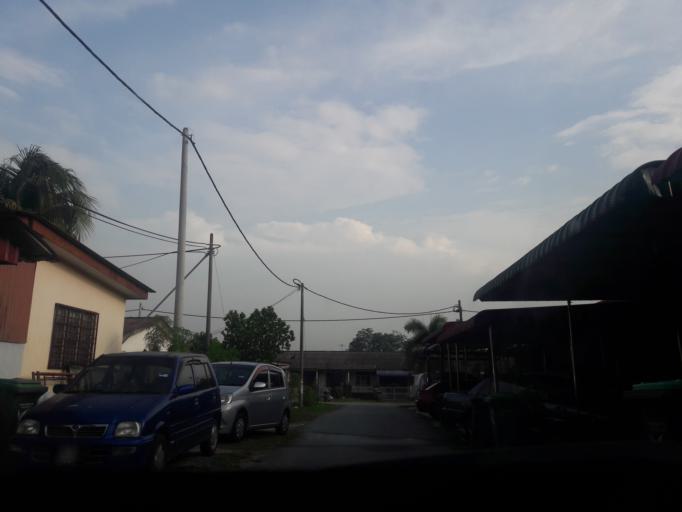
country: MY
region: Kedah
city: Kulim
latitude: 5.3780
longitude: 100.5329
